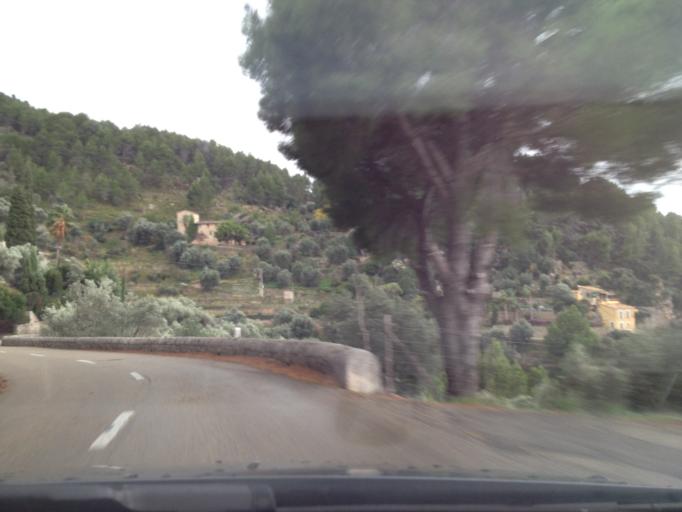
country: ES
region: Balearic Islands
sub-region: Illes Balears
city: Deia
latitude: 39.7719
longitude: 2.6685
